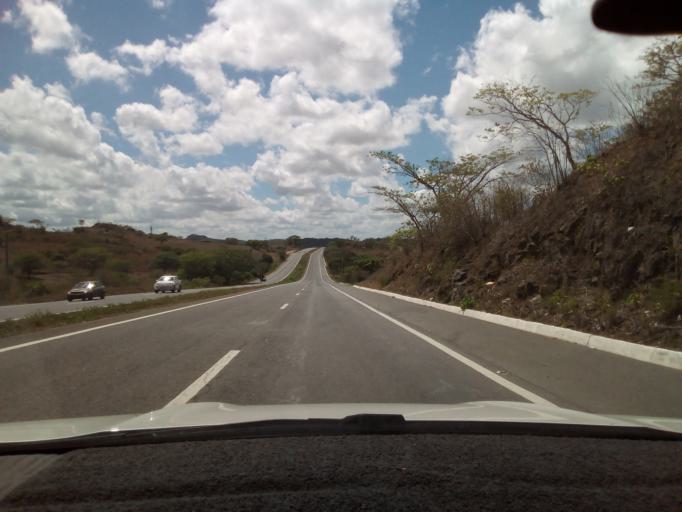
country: BR
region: Paraiba
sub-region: Massaranduba
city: Massaranduba
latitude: -7.2561
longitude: -35.8210
